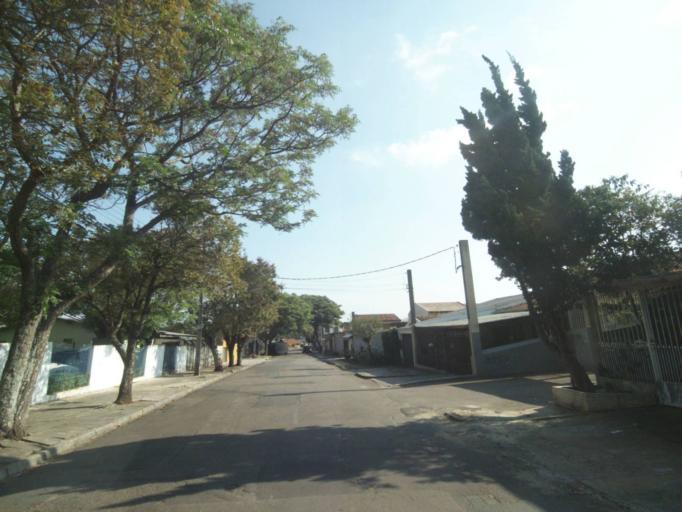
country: BR
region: Parana
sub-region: Curitiba
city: Curitiba
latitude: -25.4904
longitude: -49.3263
